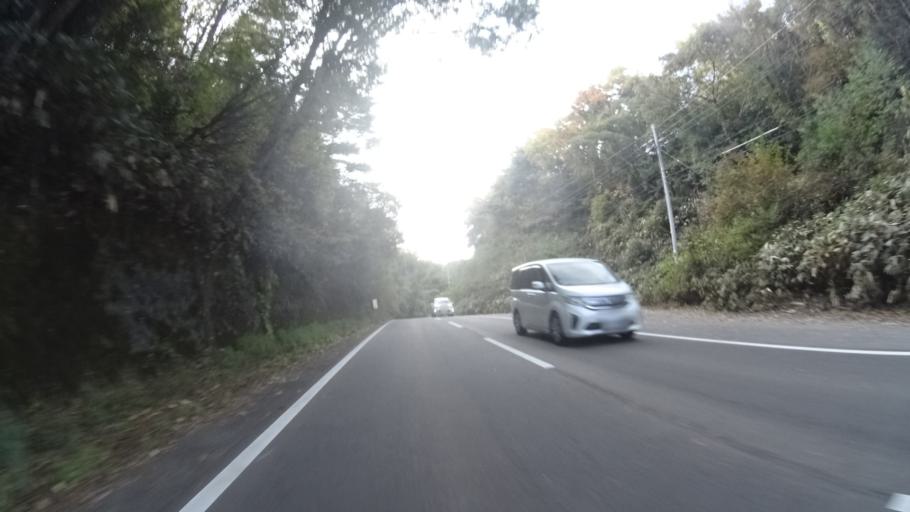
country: JP
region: Ishikawa
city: Nanao
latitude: 37.2056
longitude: 136.7086
